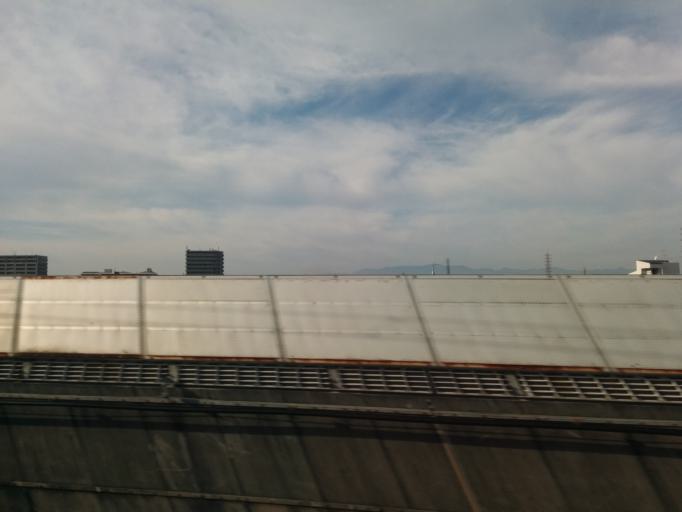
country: JP
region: Shiga Prefecture
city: Moriyama
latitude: 35.0697
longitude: 136.0318
